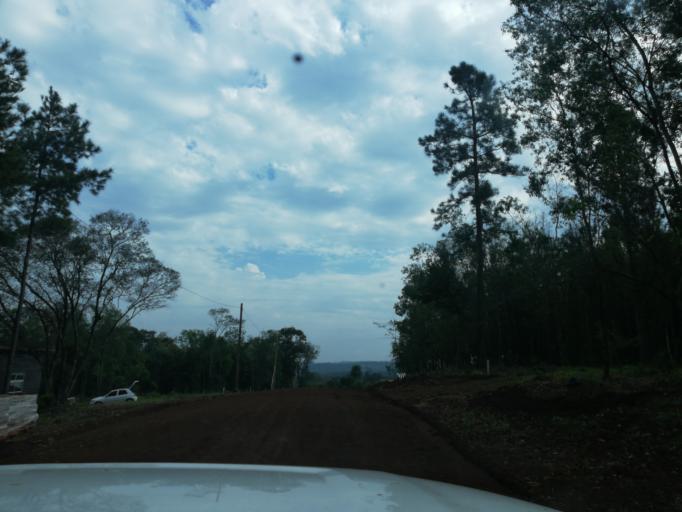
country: AR
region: Misiones
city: Cerro Azul
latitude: -27.6035
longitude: -55.4945
